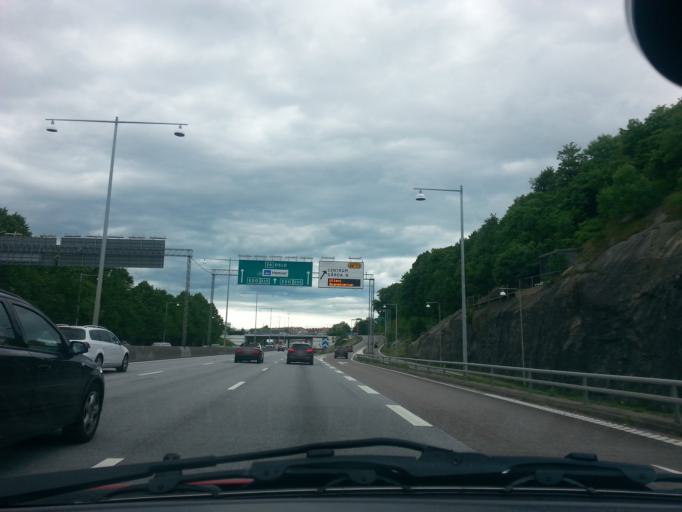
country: SE
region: Vaestra Goetaland
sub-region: Goteborg
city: Goeteborg
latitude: 57.7040
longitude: 11.9953
